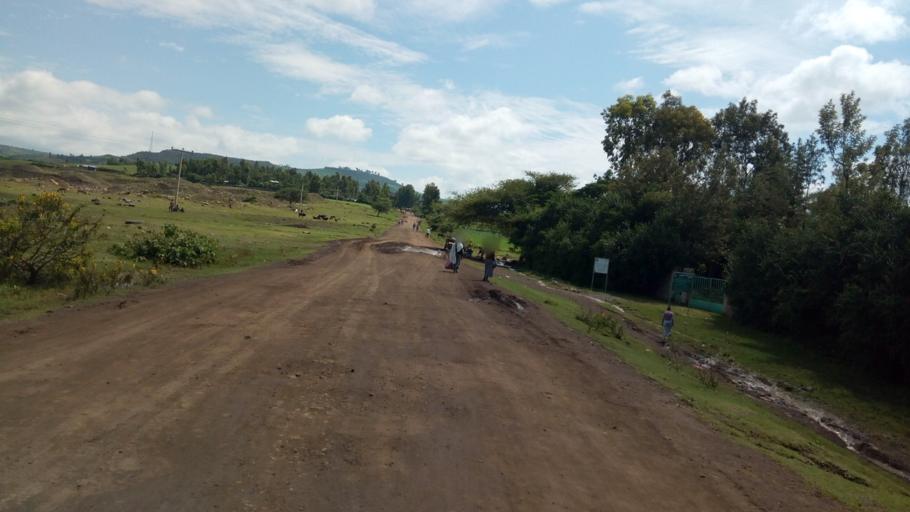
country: ET
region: Oromiya
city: Bishoftu
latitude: 8.8423
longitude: 39.0143
